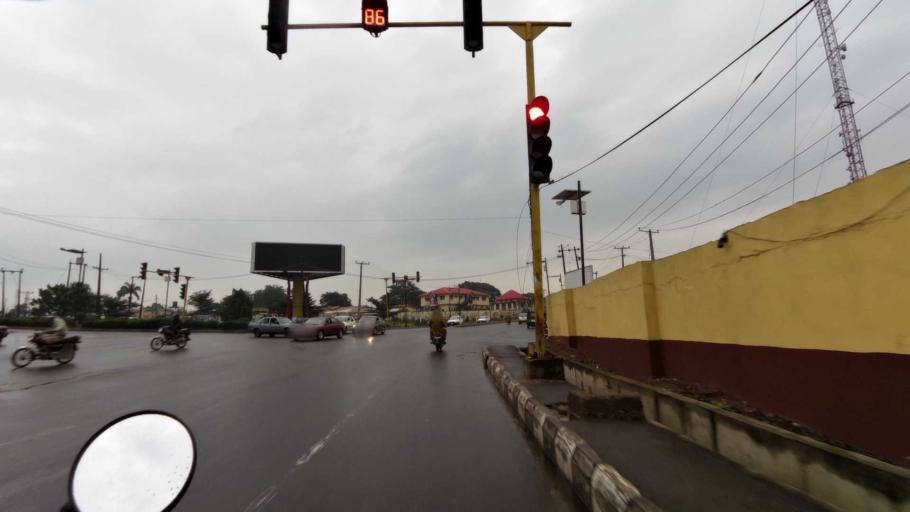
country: NG
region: Oyo
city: Ibadan
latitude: 7.3973
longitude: 3.9170
